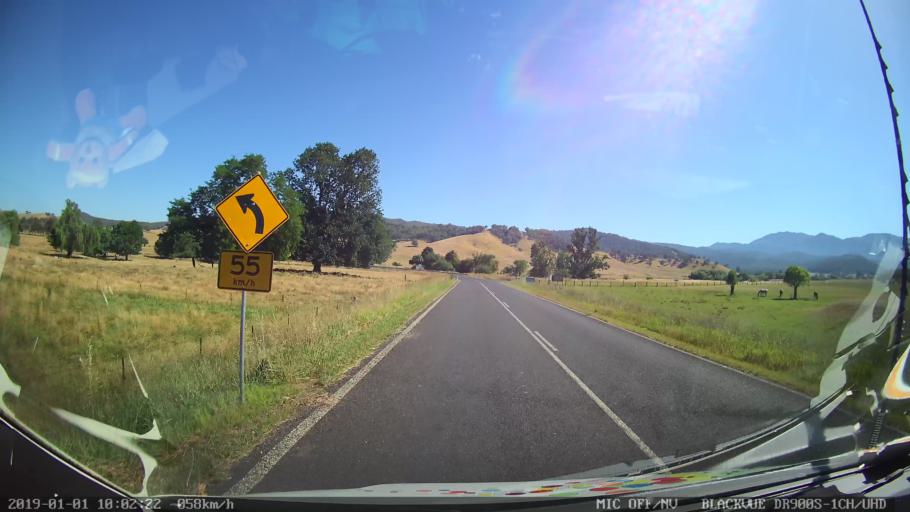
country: AU
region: New South Wales
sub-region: Snowy River
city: Jindabyne
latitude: -36.1820
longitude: 148.1020
